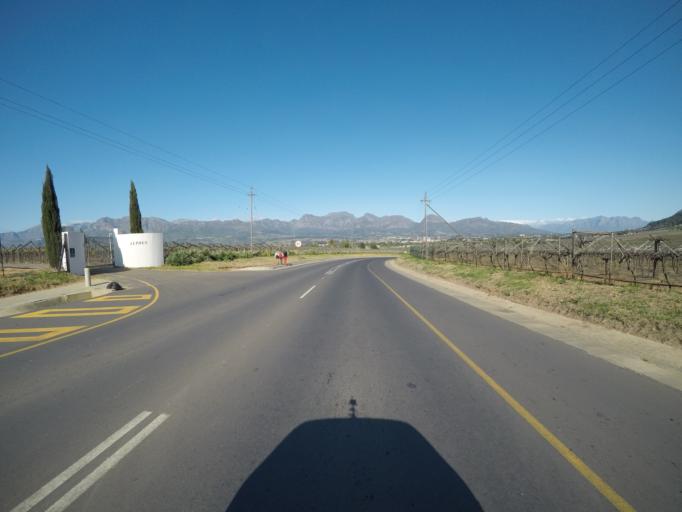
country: ZA
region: Western Cape
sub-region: Cape Winelands District Municipality
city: Noorder-Paarl
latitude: -33.6925
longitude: 18.9562
